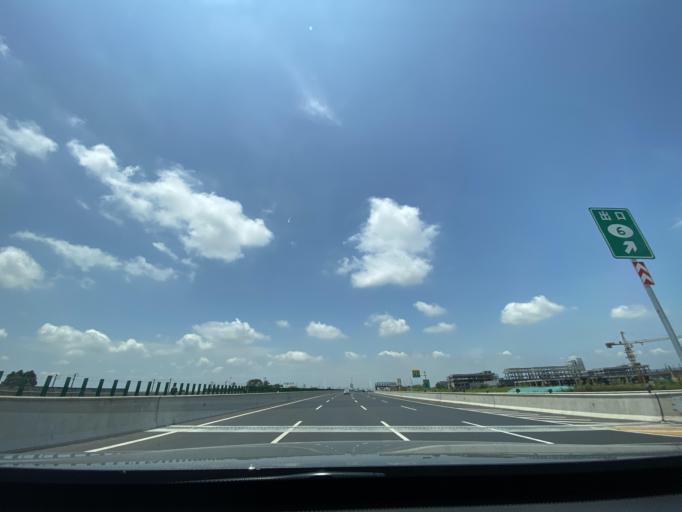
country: CN
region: Sichuan
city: Longquan
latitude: 30.5182
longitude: 104.1782
